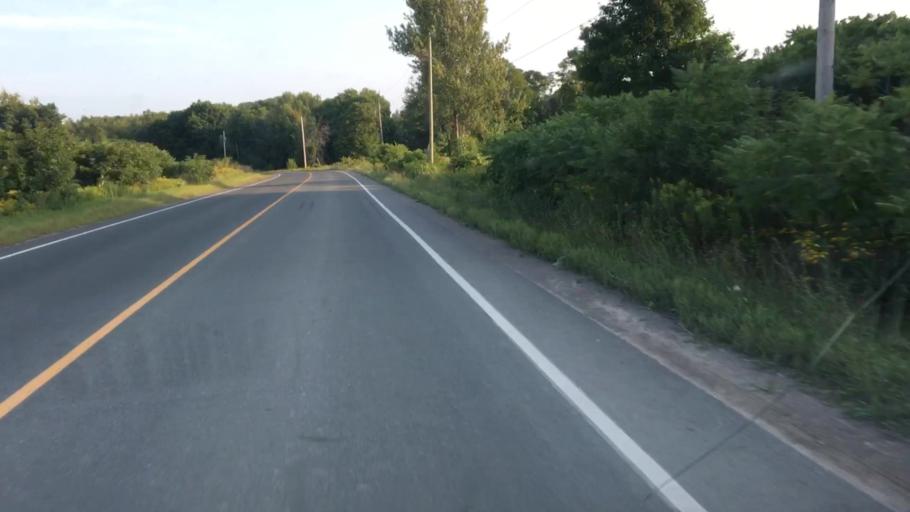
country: CA
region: Ontario
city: Quinte West
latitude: 44.0974
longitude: -77.7355
